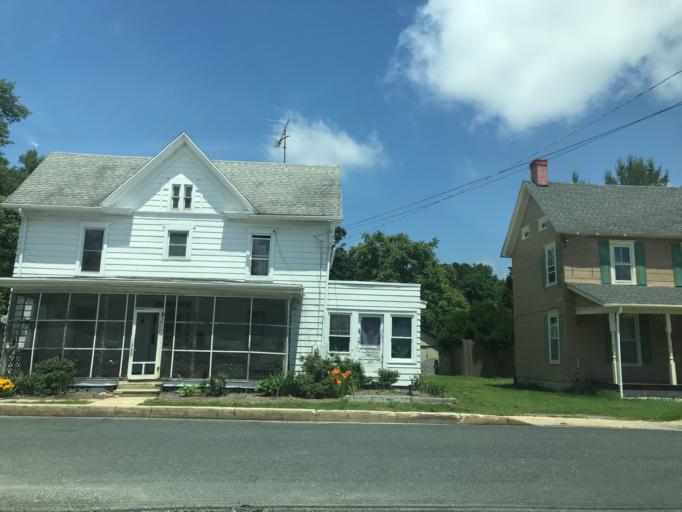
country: US
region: Maryland
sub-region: Caroline County
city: Federalsburg
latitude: 38.6952
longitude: -75.7679
